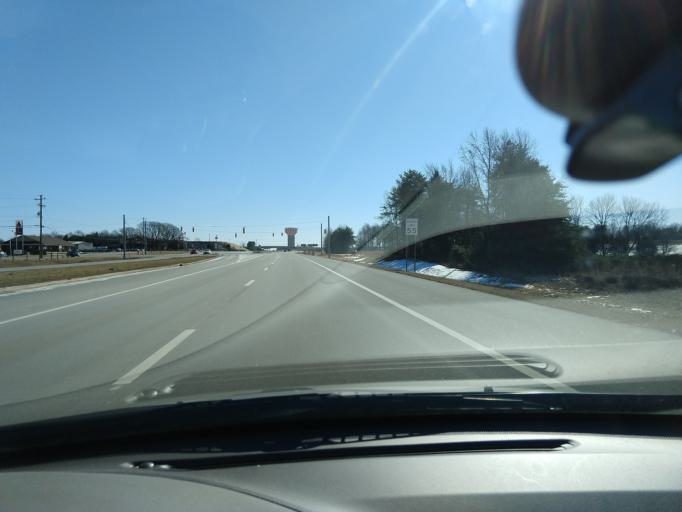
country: US
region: North Carolina
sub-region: Guilford County
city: Oak Ridge
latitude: 36.1306
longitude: -79.9642
